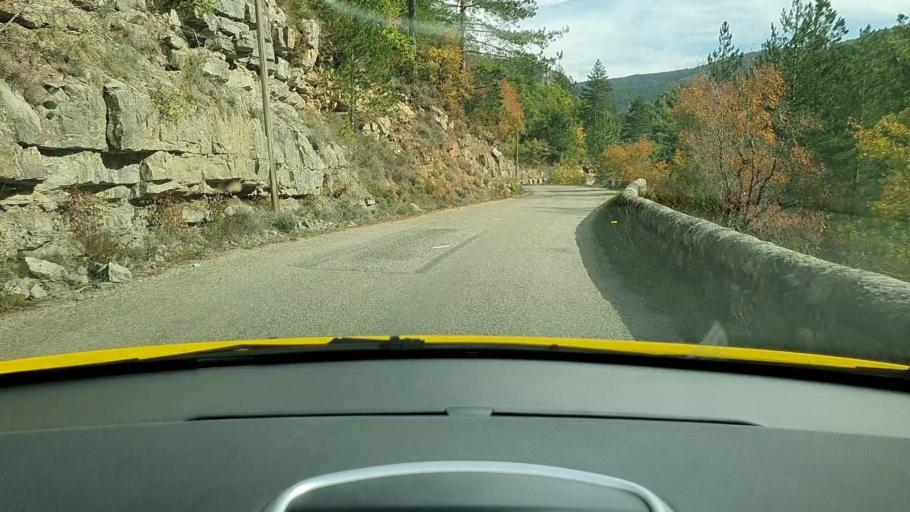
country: FR
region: Languedoc-Roussillon
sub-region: Departement de la Lozere
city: Meyrueis
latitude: 44.0766
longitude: 3.3700
